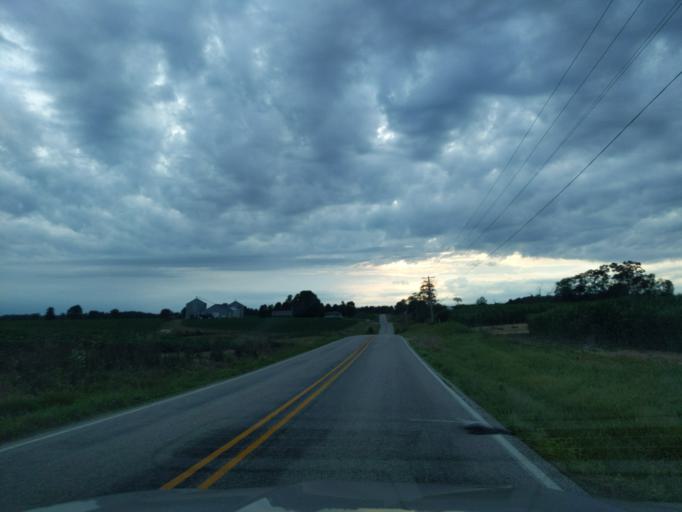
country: US
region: Indiana
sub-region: Ripley County
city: Osgood
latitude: 39.1939
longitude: -85.2278
